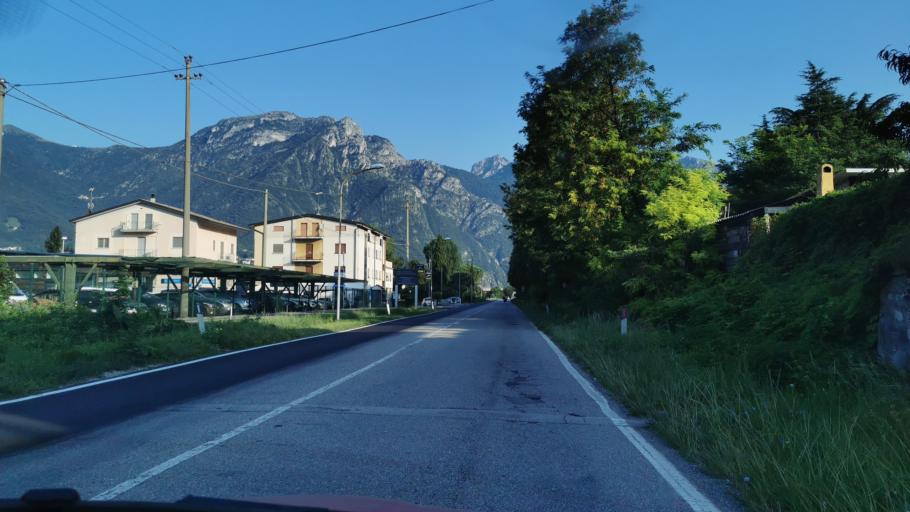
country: IT
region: Lombardy
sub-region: Provincia di Lecco
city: Sala al Barro
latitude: 45.8200
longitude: 9.3598
